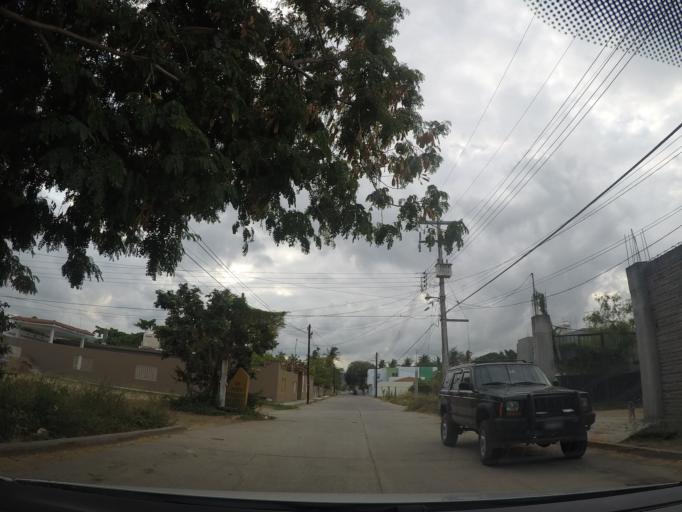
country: MX
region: Oaxaca
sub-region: Salina Cruz
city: Salina Cruz
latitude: 16.2140
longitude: -95.1951
